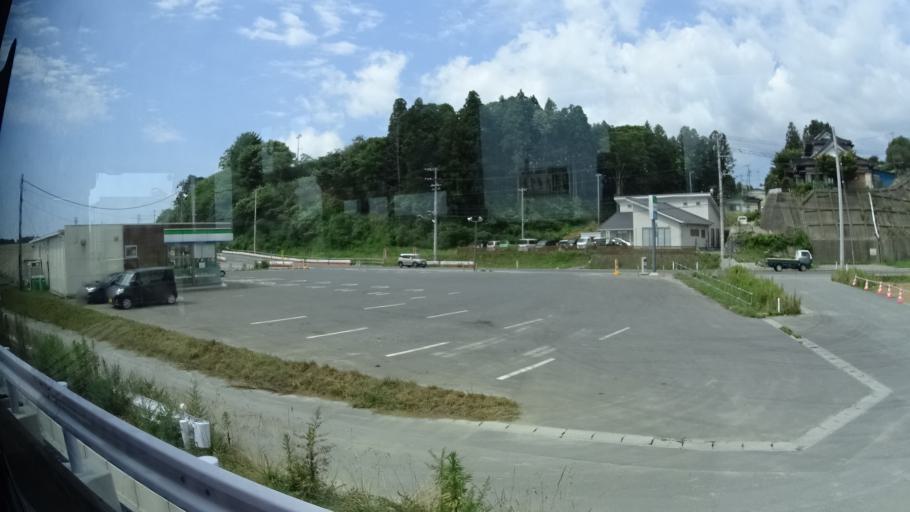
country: JP
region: Iwate
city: Ofunato
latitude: 38.8736
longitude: 141.5836
